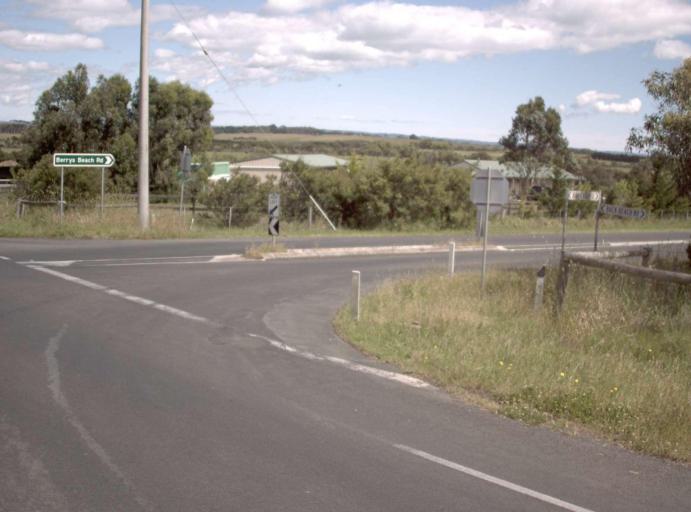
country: AU
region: Victoria
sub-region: Bass Coast
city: Phillip Island
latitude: -38.4967
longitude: 145.2016
